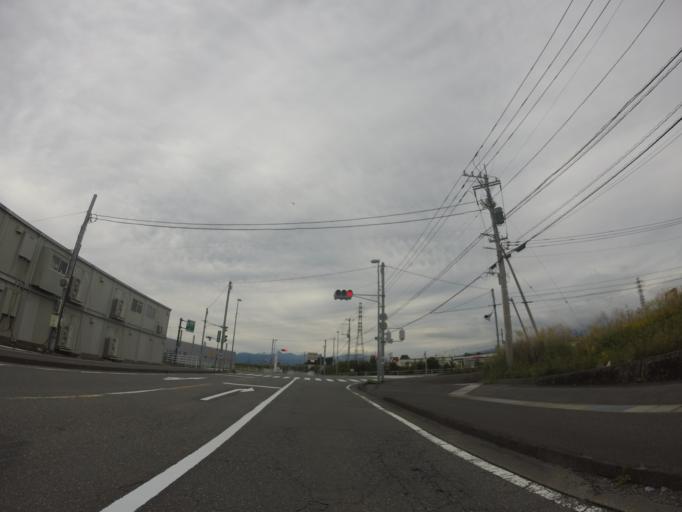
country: JP
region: Shizuoka
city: Fuji
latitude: 35.2006
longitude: 138.6735
